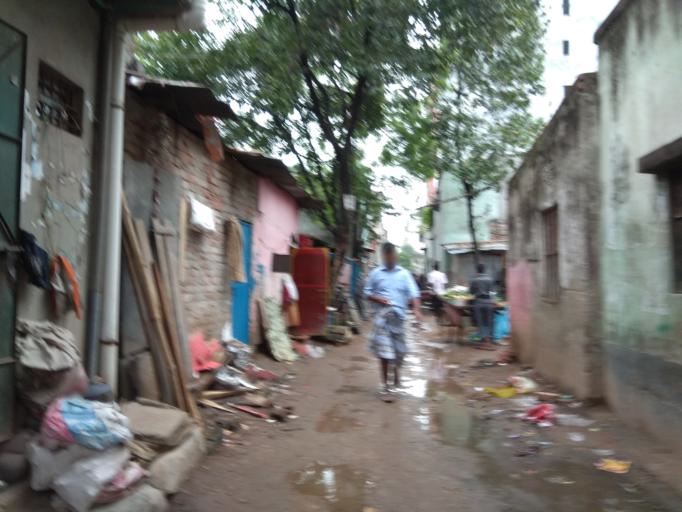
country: BD
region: Dhaka
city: Tungi
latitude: 23.8232
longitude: 90.3729
